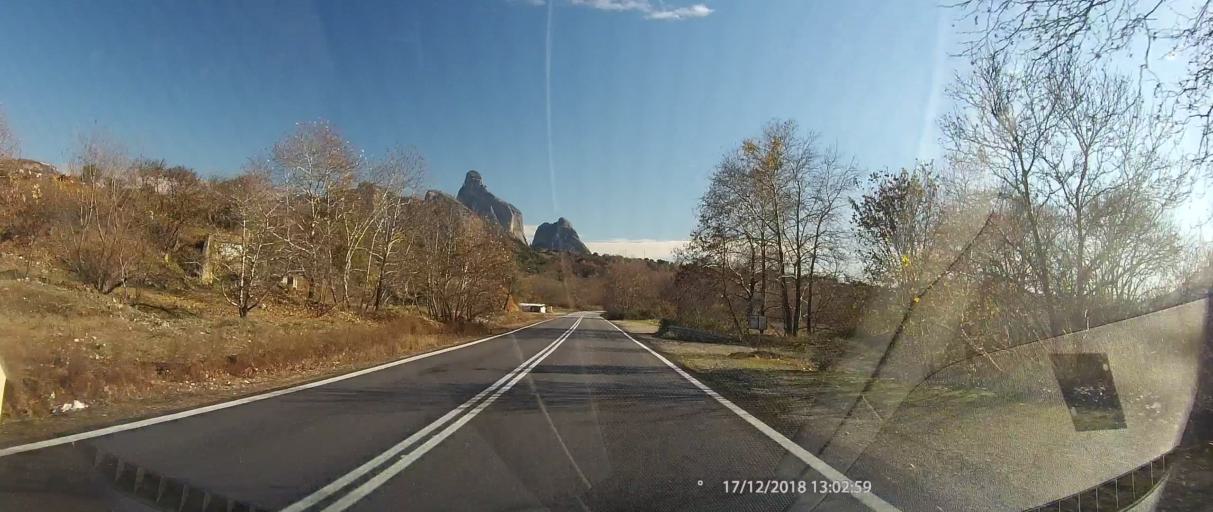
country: GR
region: Thessaly
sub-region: Trikala
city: Kastraki
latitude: 39.7166
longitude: 21.5973
